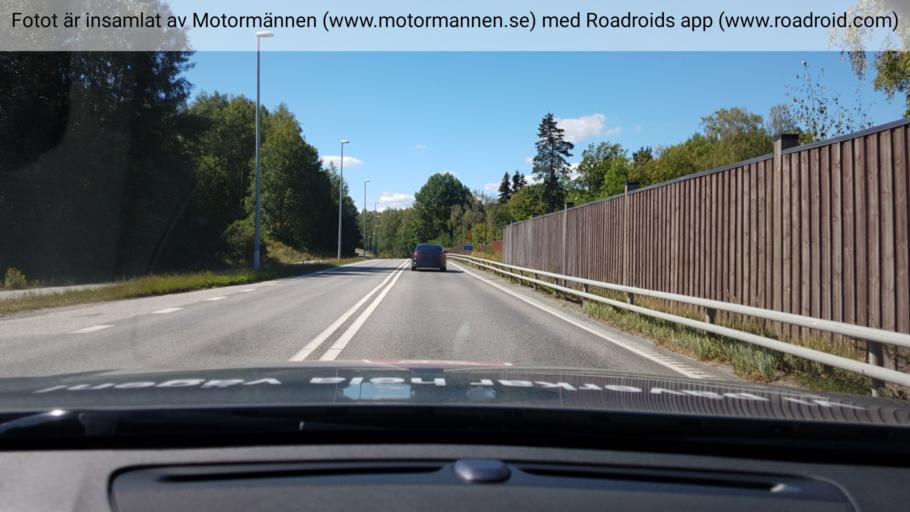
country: SE
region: Stockholm
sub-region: Tyreso Kommun
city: Bollmora
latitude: 59.2038
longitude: 18.1996
